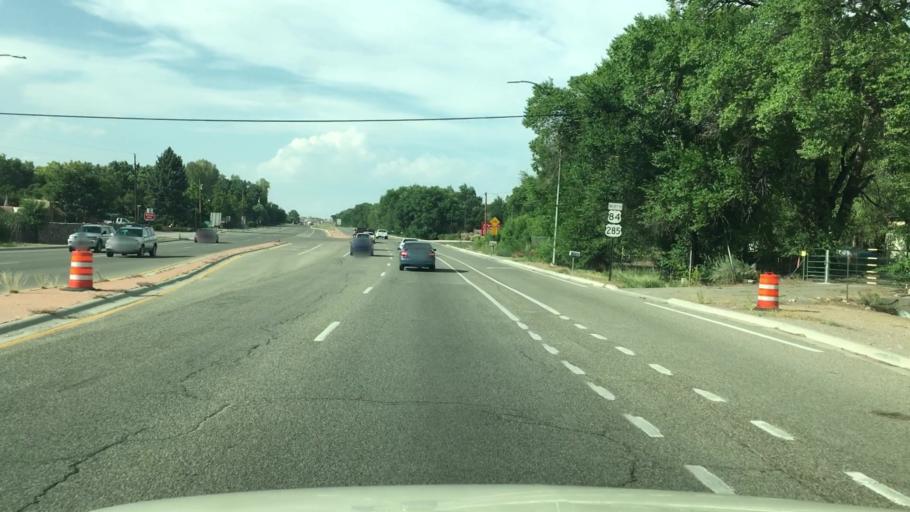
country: US
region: New Mexico
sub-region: Santa Fe County
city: Pojoaque
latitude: 35.8978
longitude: -106.0208
